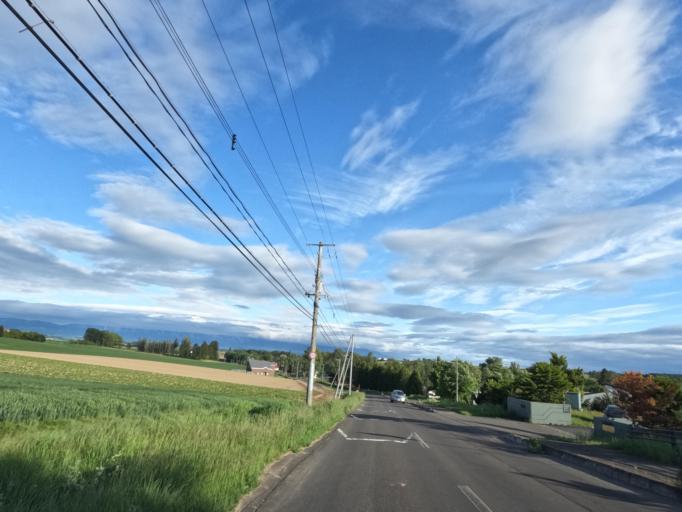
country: JP
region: Hokkaido
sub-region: Asahikawa-shi
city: Asahikawa
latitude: 43.6240
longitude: 142.4467
